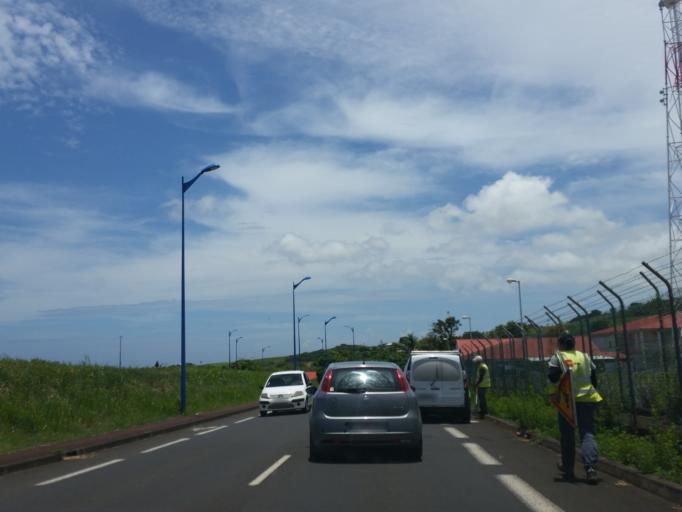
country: RE
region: Reunion
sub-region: Reunion
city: Sainte-Marie
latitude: -20.9113
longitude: 55.5164
